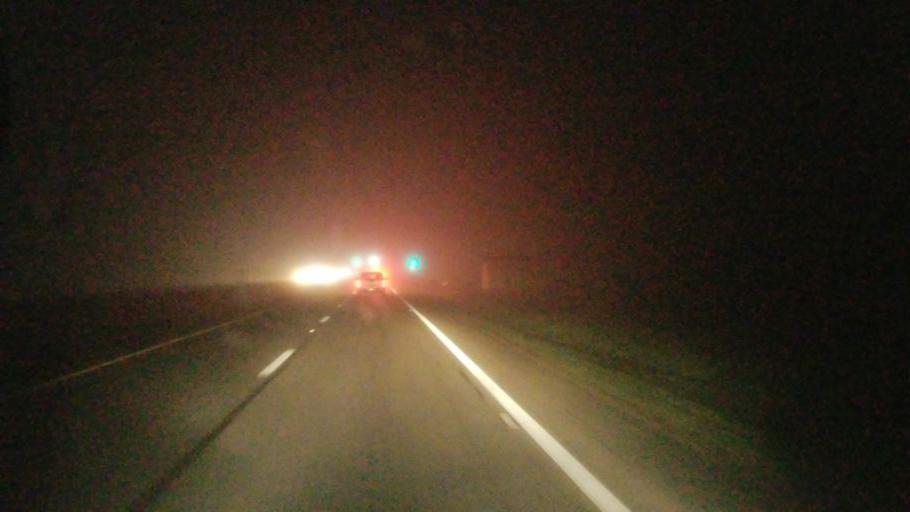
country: US
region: Ohio
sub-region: Pickaway County
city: South Bloomfield
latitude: 39.7253
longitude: -82.9867
